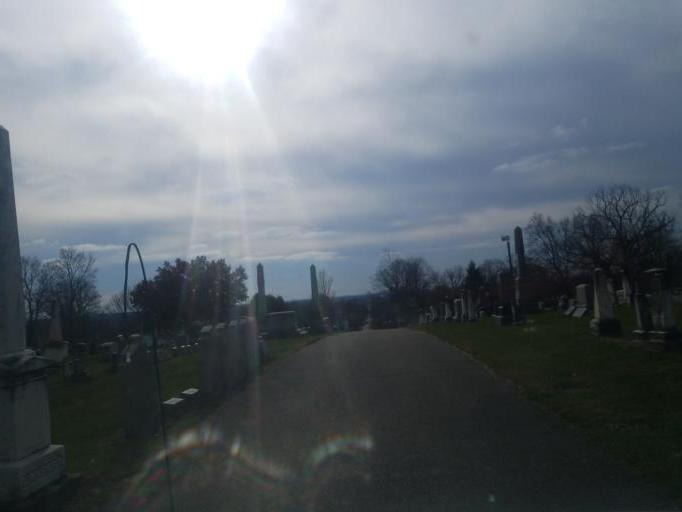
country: US
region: Ohio
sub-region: Knox County
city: Mount Vernon
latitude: 40.4036
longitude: -82.4846
